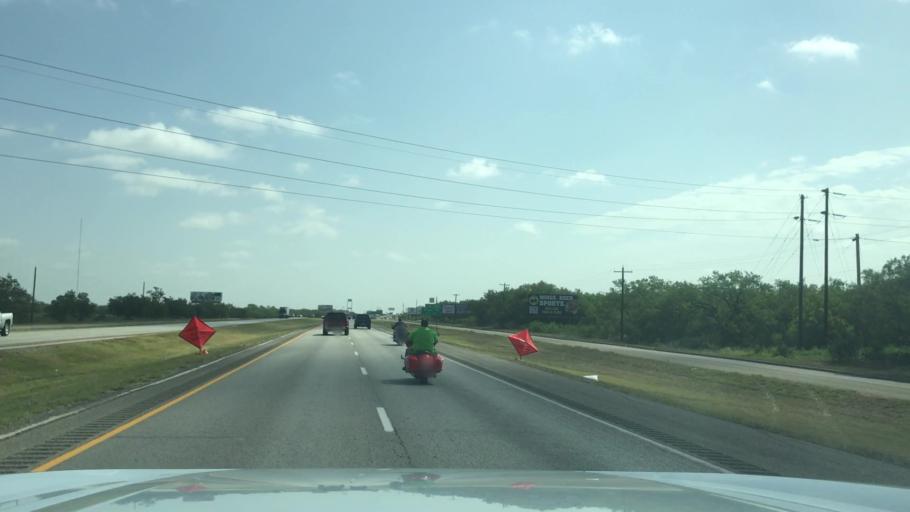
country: US
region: Texas
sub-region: Taylor County
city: Abilene
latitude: 32.4863
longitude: -99.7593
